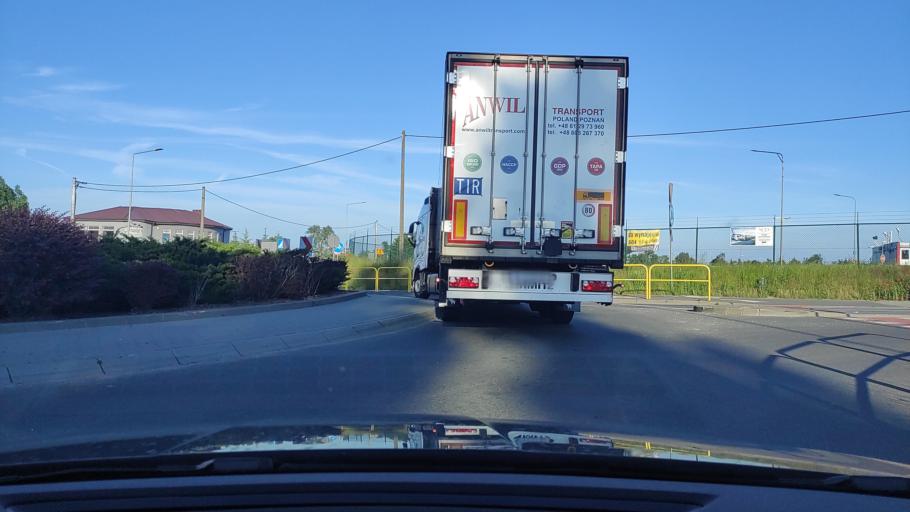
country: PL
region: Greater Poland Voivodeship
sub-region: Powiat poznanski
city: Kornik
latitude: 52.3098
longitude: 17.0671
